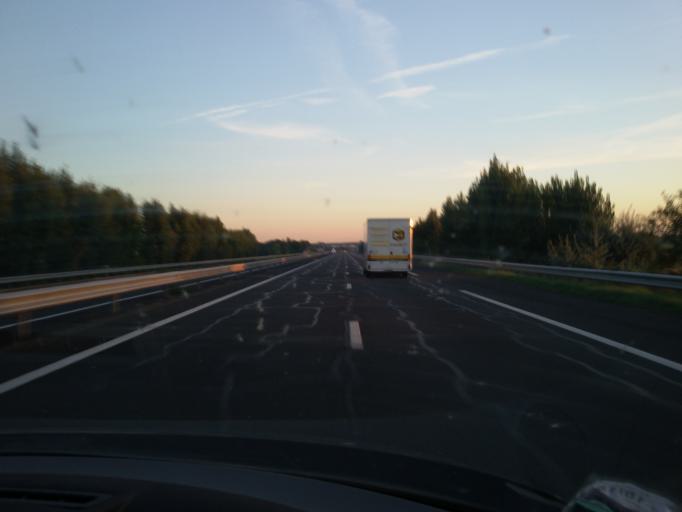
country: FR
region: Auvergne
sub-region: Departement du Puy-de-Dome
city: Menetrol
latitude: 45.8757
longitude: 3.1556
